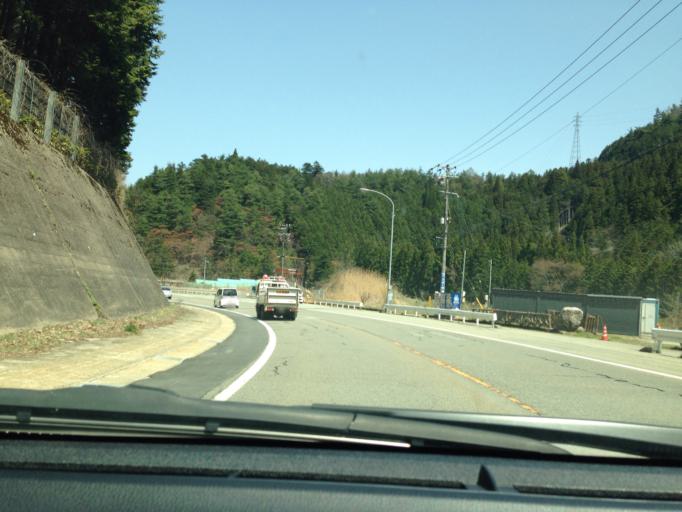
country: JP
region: Gifu
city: Takayama
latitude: 36.1014
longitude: 137.2633
